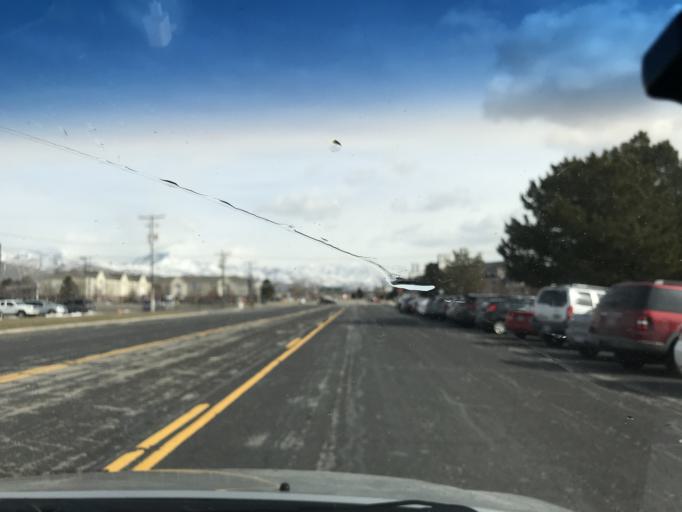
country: US
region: Utah
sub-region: Salt Lake County
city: Salt Lake City
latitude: 40.7714
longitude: -111.9556
